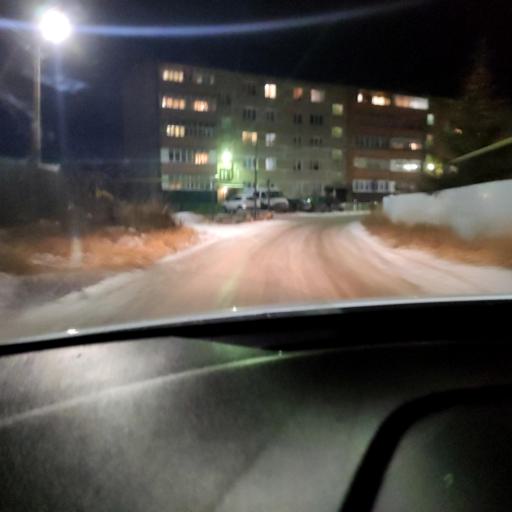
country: RU
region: Tatarstan
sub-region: Gorod Kazan'
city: Kazan
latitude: 55.7184
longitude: 49.0973
